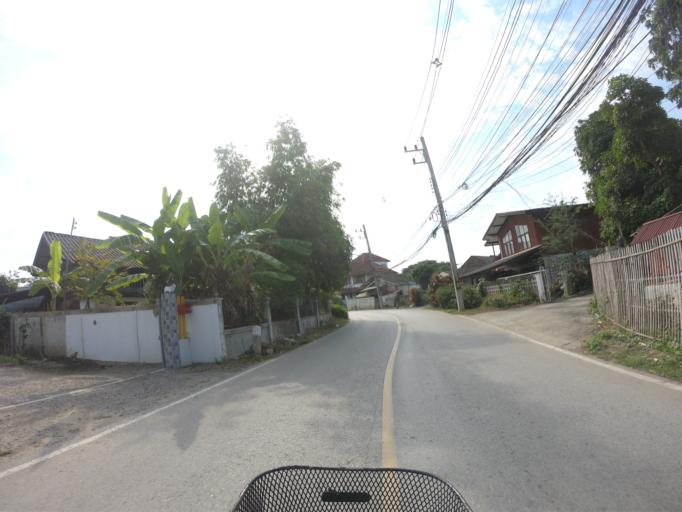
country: TH
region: Chiang Mai
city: Saraphi
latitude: 18.7288
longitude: 99.0626
